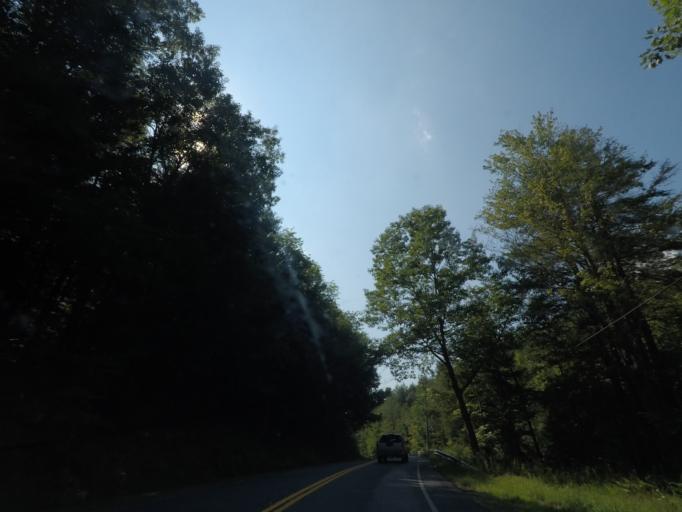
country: US
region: New York
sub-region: Rensselaer County
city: Poestenkill
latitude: 42.7091
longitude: -73.5081
